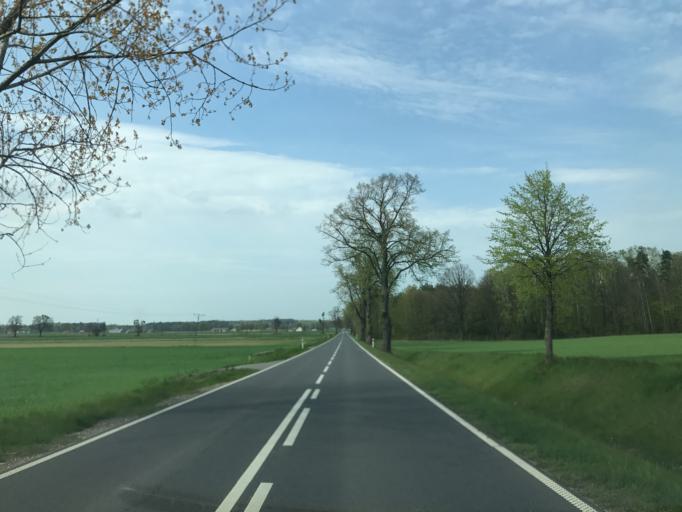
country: PL
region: Warmian-Masurian Voivodeship
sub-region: Powiat dzialdowski
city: Lidzbark
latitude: 53.3587
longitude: 19.8203
